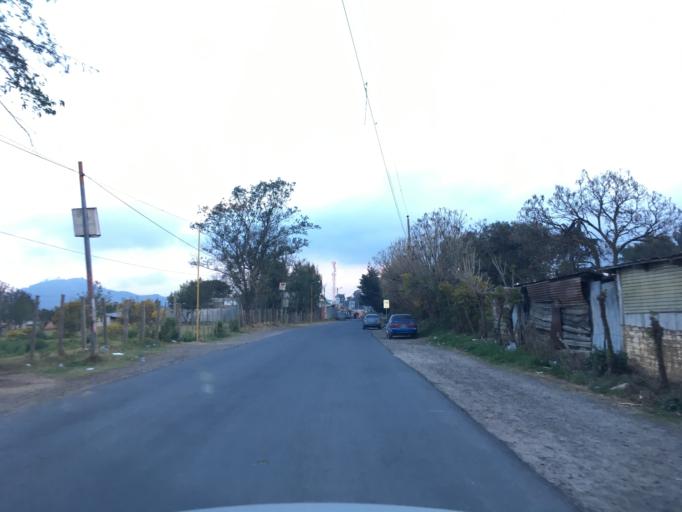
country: GT
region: Chimaltenango
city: Tecpan Guatemala
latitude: 14.7560
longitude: -90.9998
